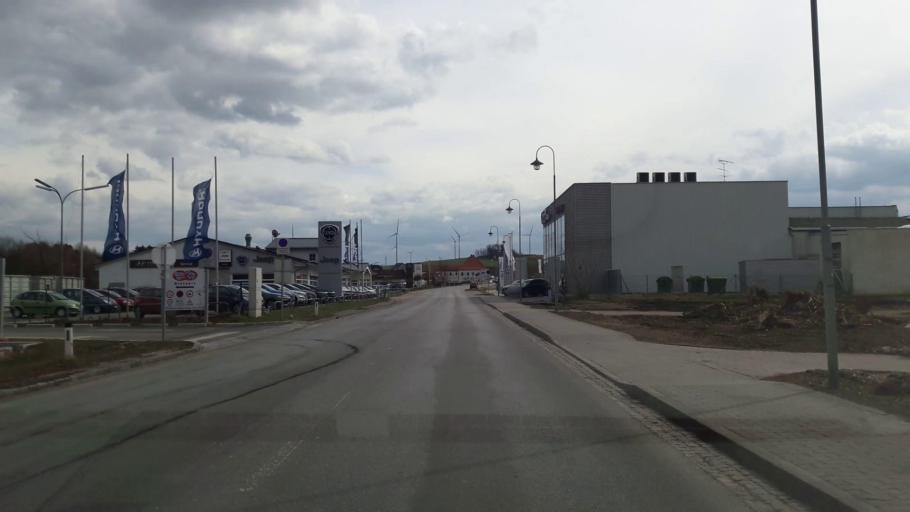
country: AT
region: Lower Austria
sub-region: Politischer Bezirk Mistelbach
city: Mistelbach
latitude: 48.5594
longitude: 16.5618
